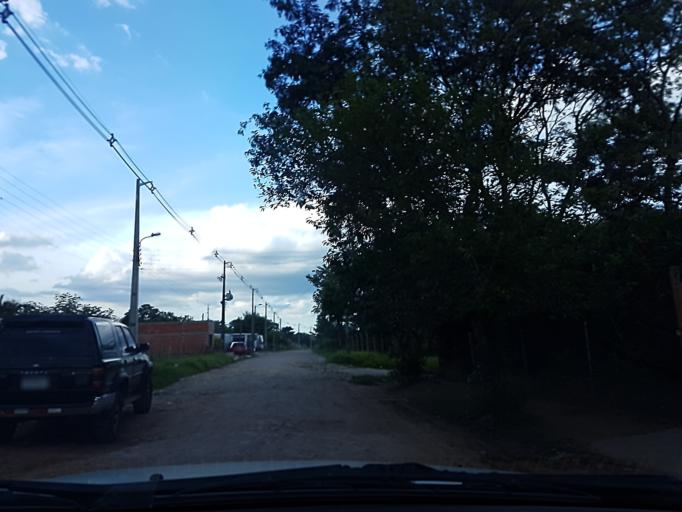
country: PY
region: Central
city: Colonia Mariano Roque Alonso
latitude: -25.2393
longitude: -57.5279
